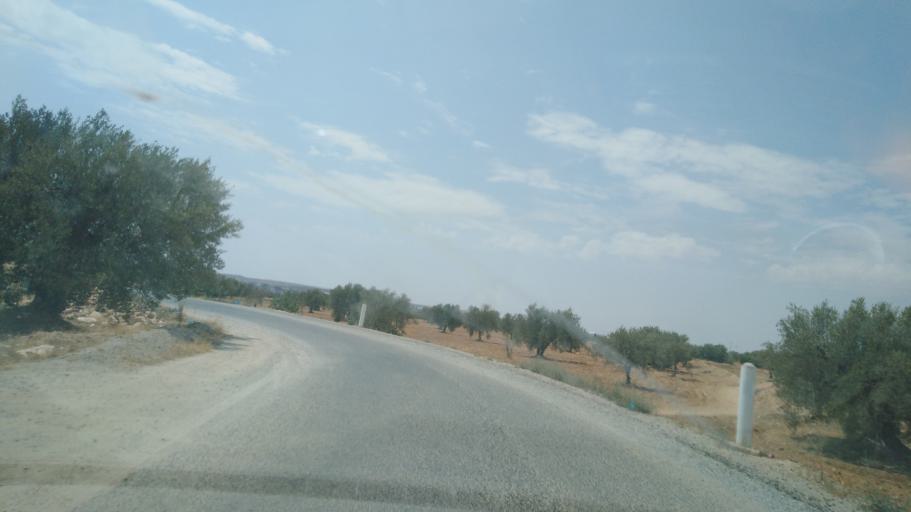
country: TN
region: Safaqis
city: Sfax
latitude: 34.7475
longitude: 10.5550
